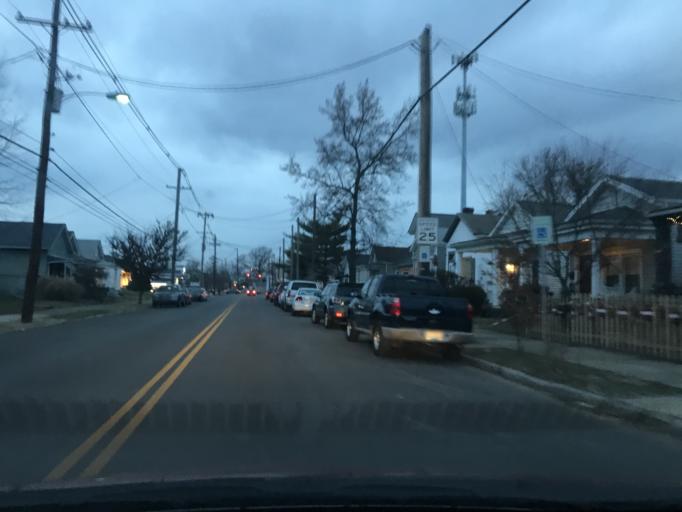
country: US
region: Kentucky
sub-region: Jefferson County
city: Audubon Park
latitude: 38.2239
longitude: -85.7408
